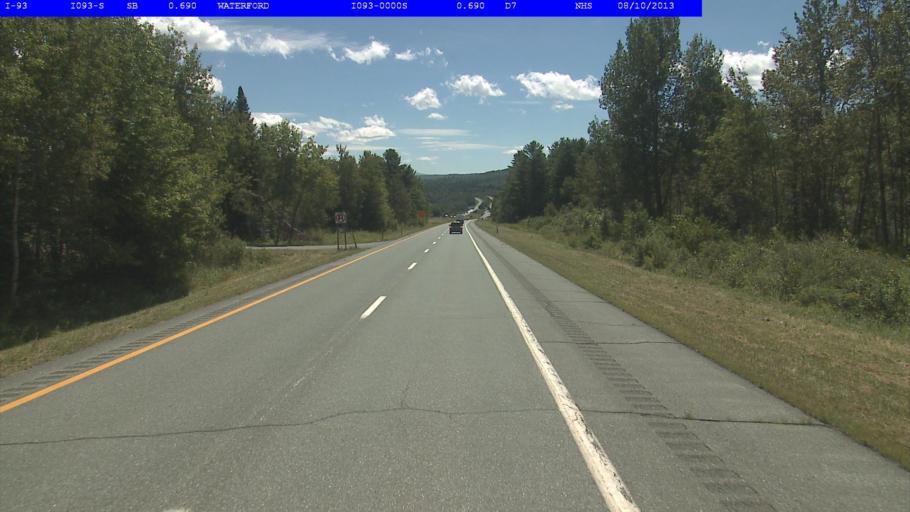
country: US
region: New Hampshire
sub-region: Grafton County
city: Littleton
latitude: 44.3528
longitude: -71.8955
